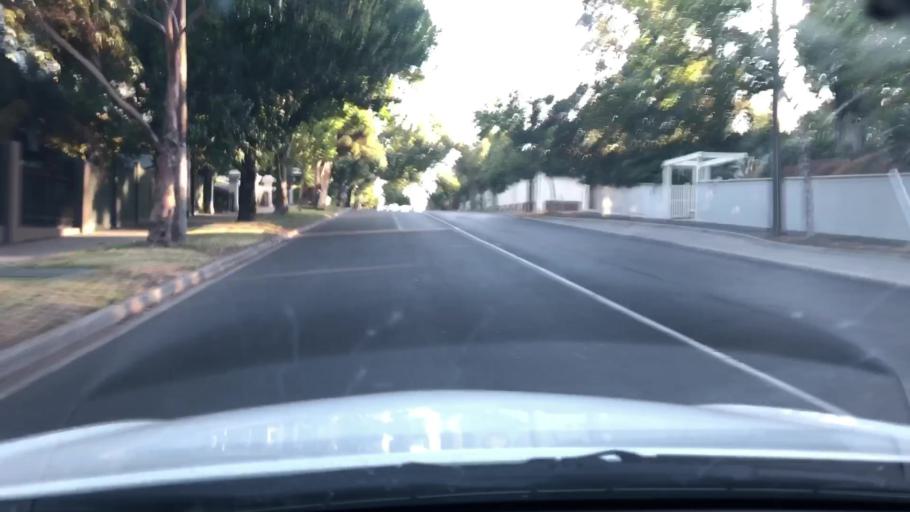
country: AU
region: Victoria
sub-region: Stonnington
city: Toorak
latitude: -37.8381
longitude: 145.0052
